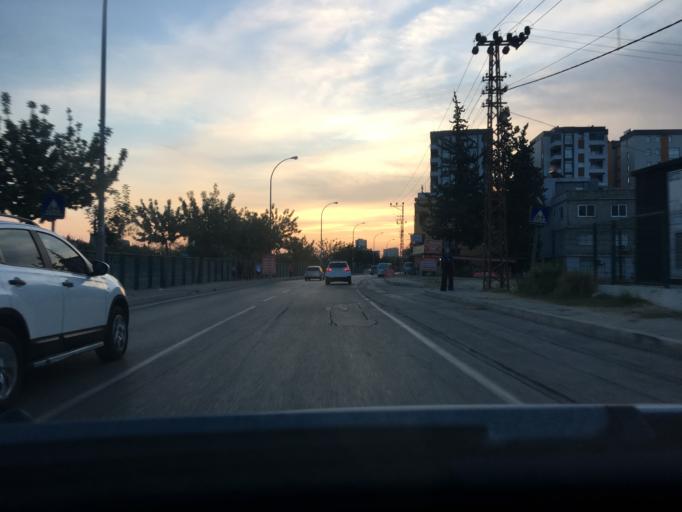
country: TR
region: Adana
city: Seyhan
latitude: 37.0109
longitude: 35.2934
